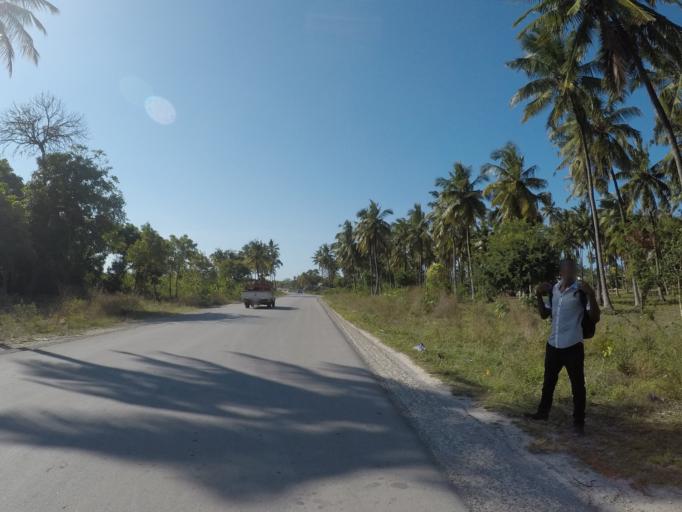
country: TZ
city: Kiwengwa
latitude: -6.1464
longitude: 39.5144
